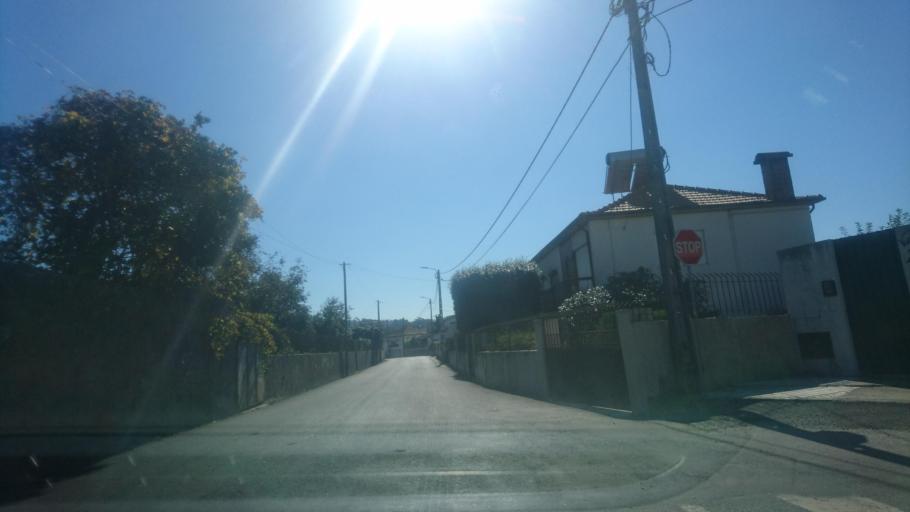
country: PT
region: Aveiro
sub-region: Santa Maria da Feira
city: Lamas
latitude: 40.9864
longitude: -8.5718
